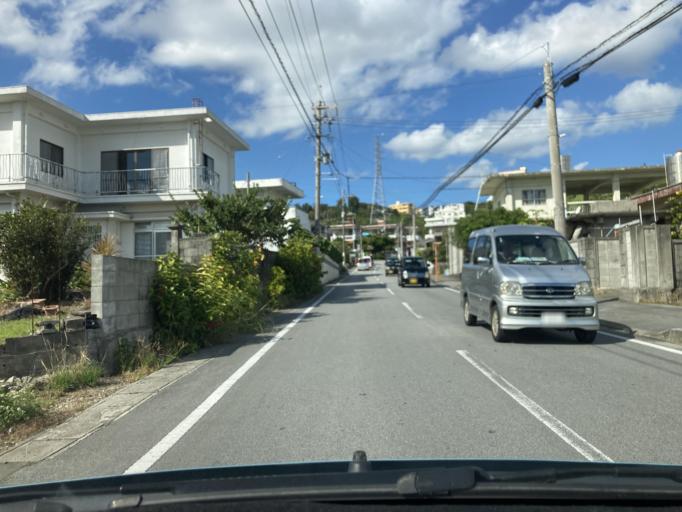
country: JP
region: Okinawa
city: Gushikawa
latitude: 26.3481
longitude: 127.8465
